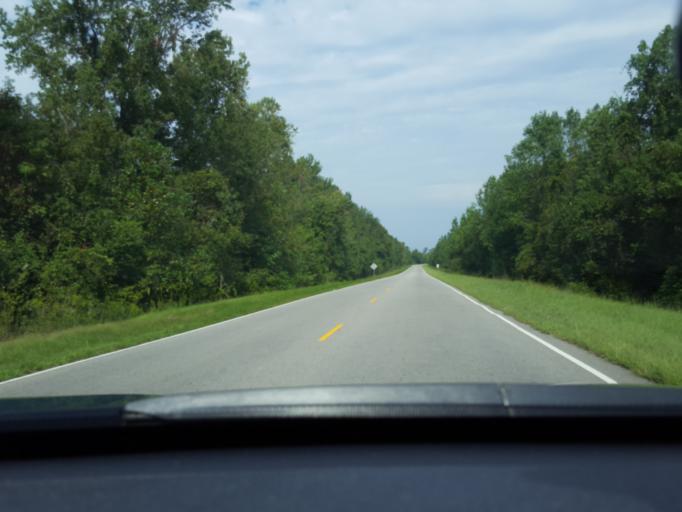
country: US
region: North Carolina
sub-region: Washington County
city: Plymouth
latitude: 35.9248
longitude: -76.7346
